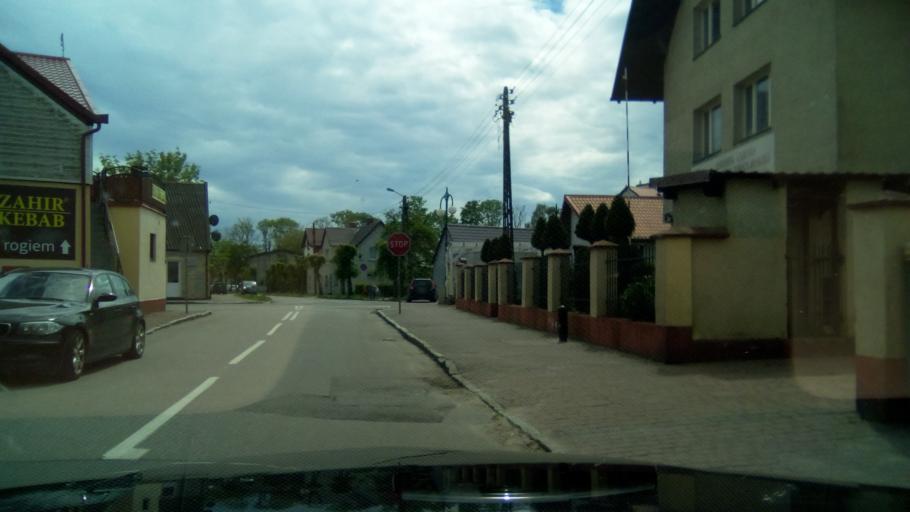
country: PL
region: Pomeranian Voivodeship
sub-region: Powiat leborski
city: Leba
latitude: 54.7586
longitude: 17.5543
